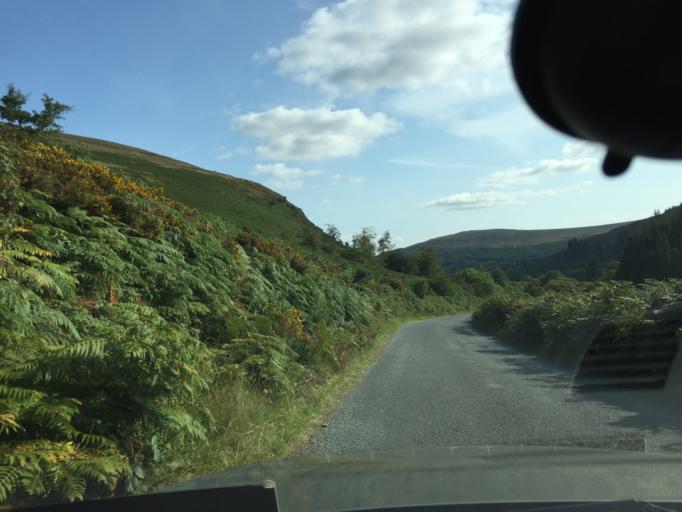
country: IE
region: Leinster
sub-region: Wicklow
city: Rathdrum
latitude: 53.0553
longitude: -6.3310
